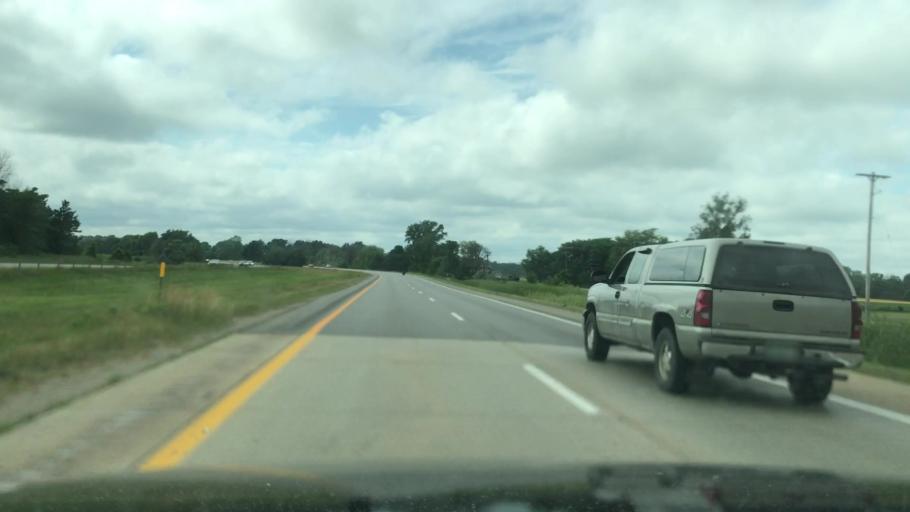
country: US
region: Michigan
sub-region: Ottawa County
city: Coopersville
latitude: 43.0675
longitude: -85.9775
